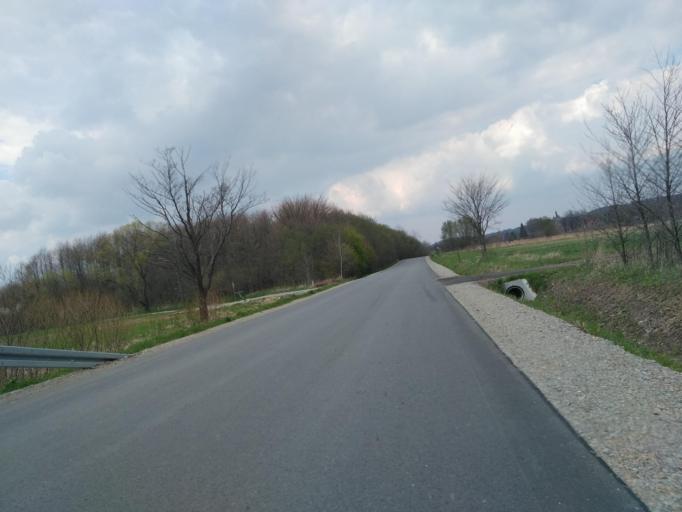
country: PL
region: Subcarpathian Voivodeship
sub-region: Powiat sanocki
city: Strachocina
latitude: 49.5931
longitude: 22.1013
